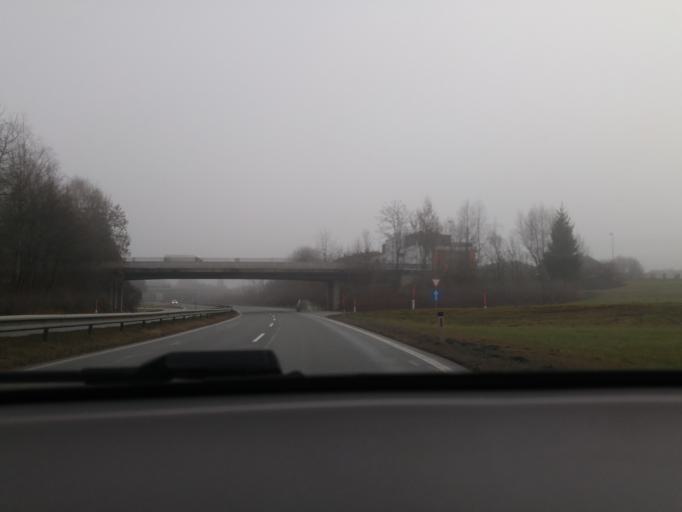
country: AT
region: Salzburg
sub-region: Politischer Bezirk Zell am See
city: Bruck an der Grossglocknerstrasse
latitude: 47.2800
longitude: 12.8235
